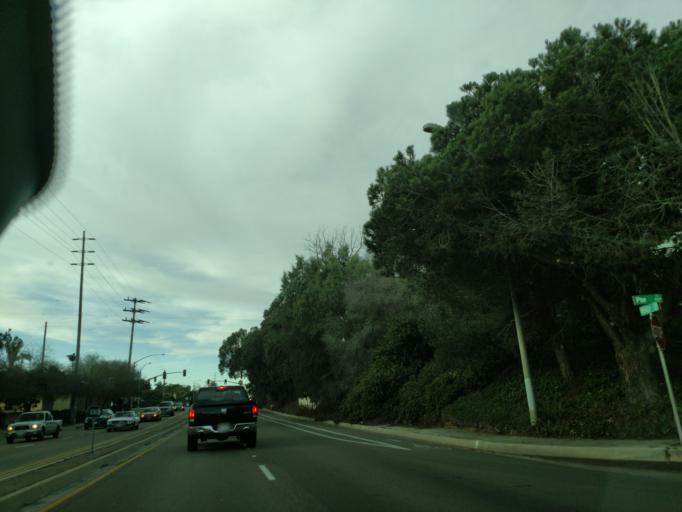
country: US
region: California
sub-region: San Diego County
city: Coronado
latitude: 32.7361
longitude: -117.2301
